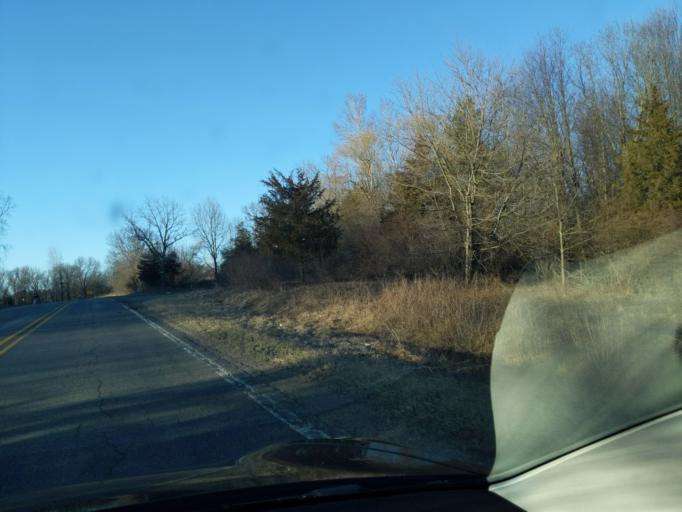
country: US
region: Michigan
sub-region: Washtenaw County
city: Chelsea
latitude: 42.4109
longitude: -84.0445
